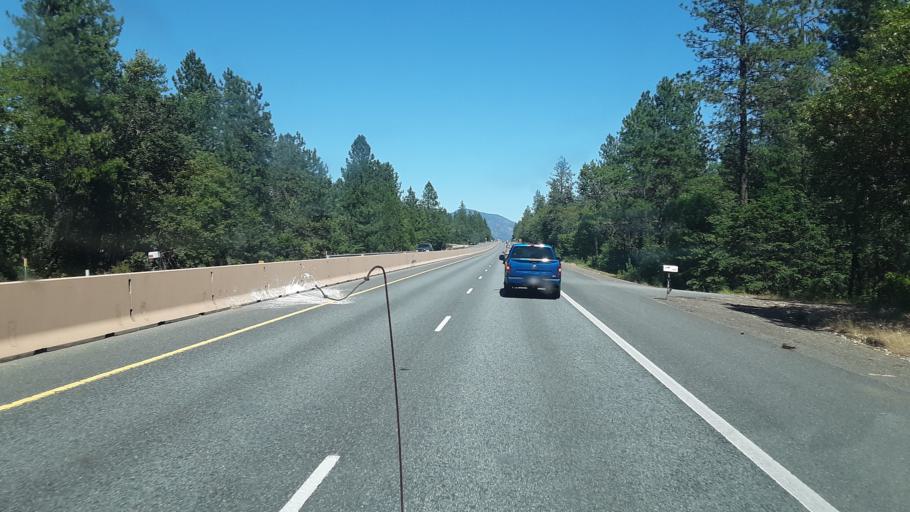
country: US
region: Oregon
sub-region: Josephine County
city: Redwood
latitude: 42.4127
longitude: -123.4101
